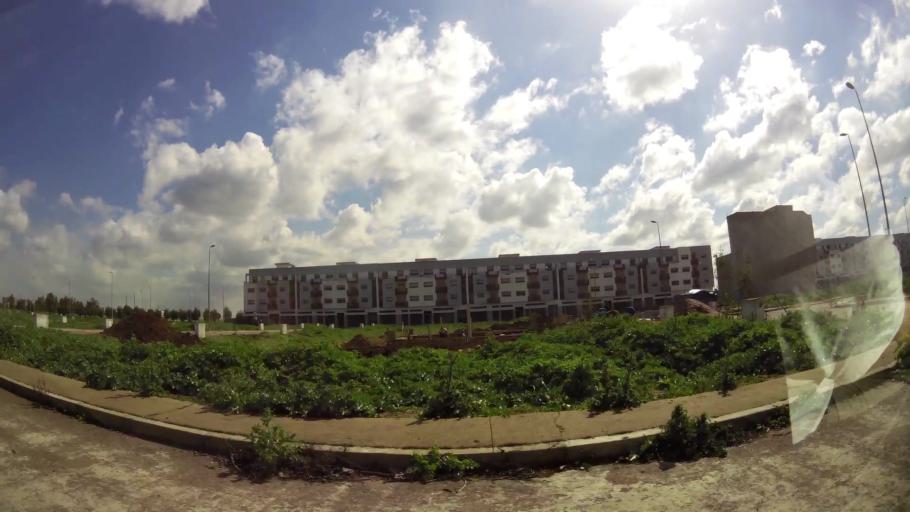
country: MA
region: Grand Casablanca
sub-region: Mediouna
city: Mediouna
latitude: 33.4494
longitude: -7.5054
